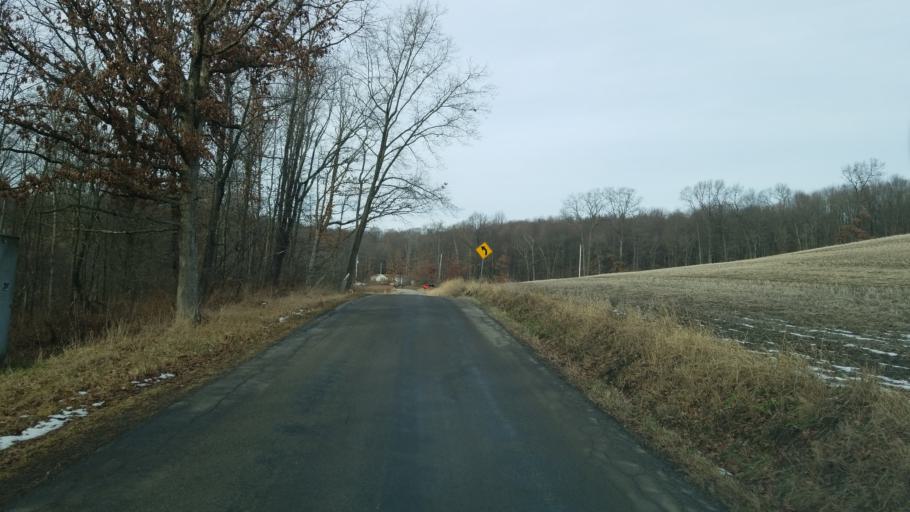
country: US
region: Pennsylvania
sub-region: Jefferson County
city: Punxsutawney
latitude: 40.8555
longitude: -79.0122
